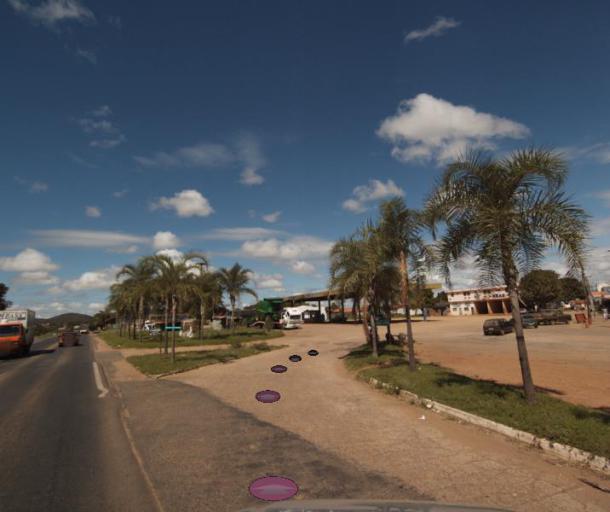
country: BR
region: Goias
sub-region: Uruacu
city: Uruacu
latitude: -14.5262
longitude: -49.1594
